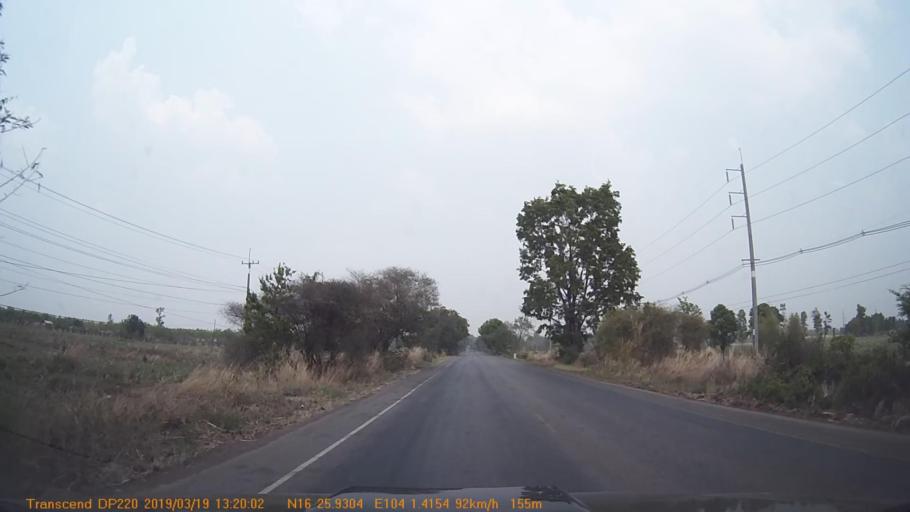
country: TH
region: Kalasin
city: Kuchinarai
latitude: 16.4327
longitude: 104.0238
